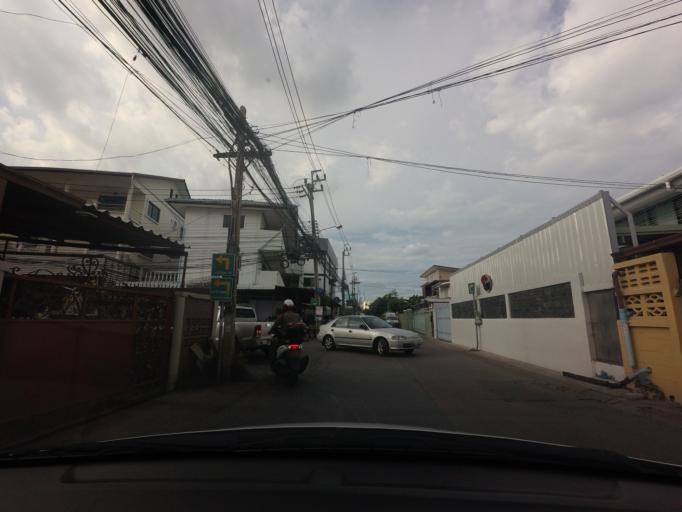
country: TH
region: Bangkok
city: Lak Si
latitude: 13.8917
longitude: 100.5807
